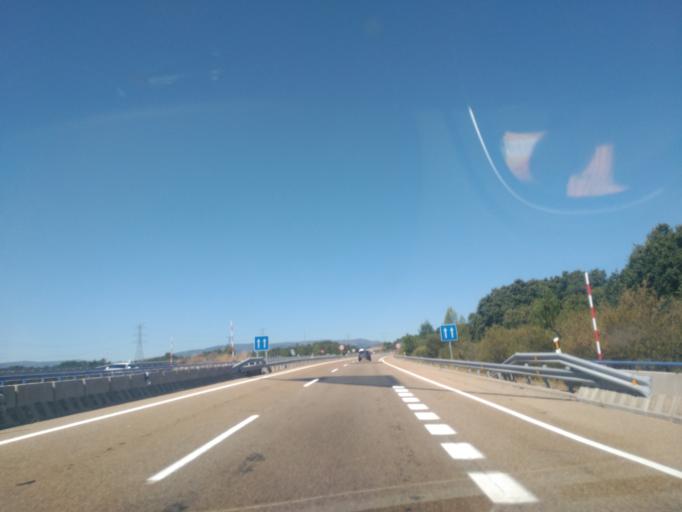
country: ES
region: Castille and Leon
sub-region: Provincia de Zamora
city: Palacios de Sanabria
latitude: 42.0535
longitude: -6.5559
